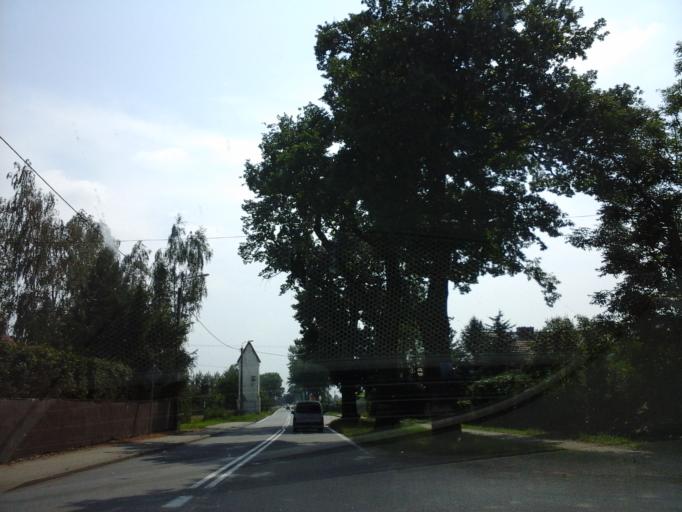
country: PL
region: Lower Silesian Voivodeship
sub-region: Powiat wroclawski
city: Zorawina
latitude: 50.9945
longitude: 17.0686
